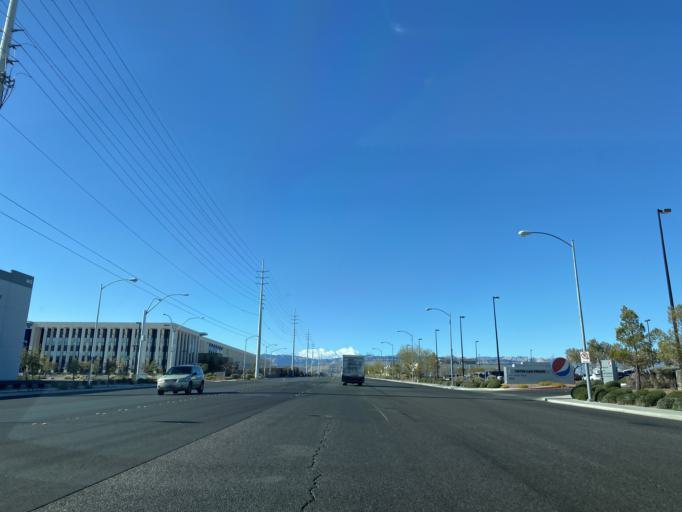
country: US
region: Nevada
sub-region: Clark County
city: Spring Valley
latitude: 36.0709
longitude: -115.2325
